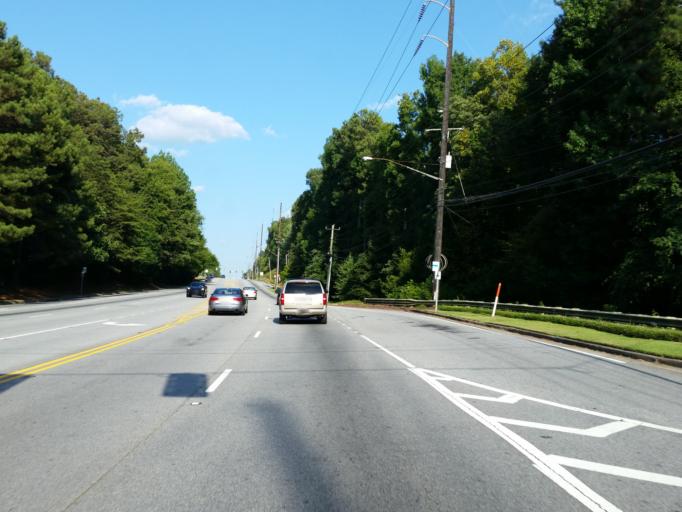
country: US
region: Georgia
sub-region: Cobb County
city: Vinings
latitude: 33.8643
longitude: -84.4497
